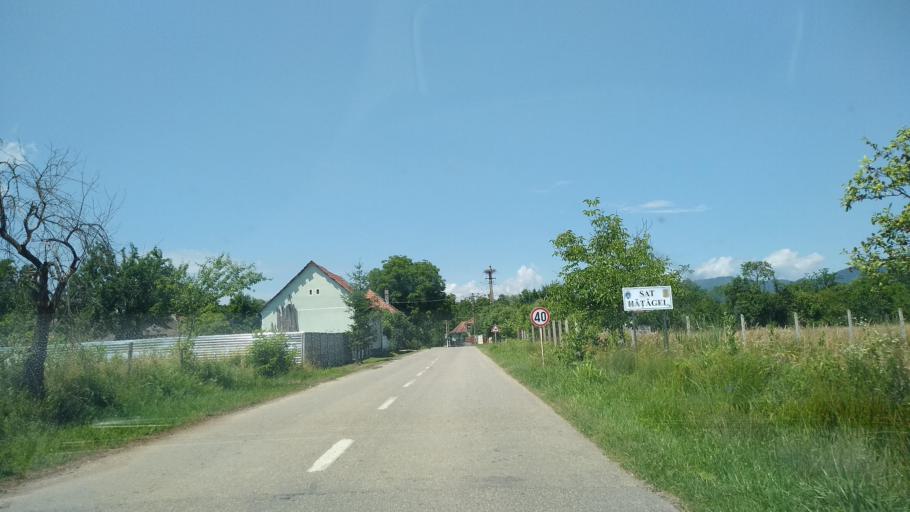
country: RO
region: Hunedoara
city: Densus
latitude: 45.5771
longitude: 22.8411
